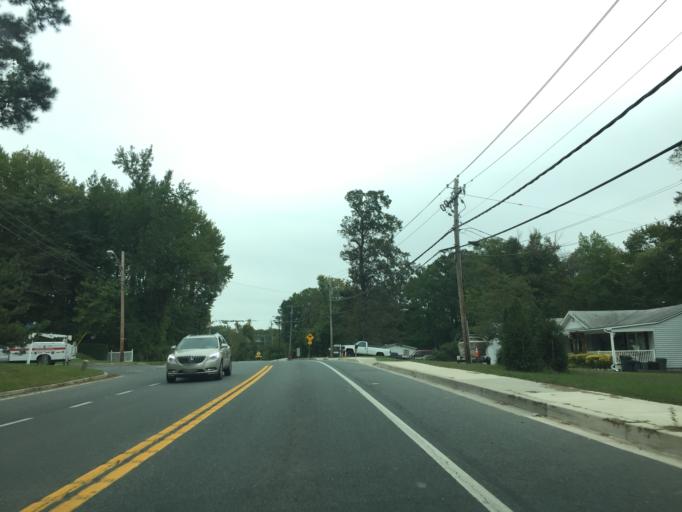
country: US
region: Maryland
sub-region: Baltimore County
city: Bowleys Quarters
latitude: 39.3406
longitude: -76.3986
